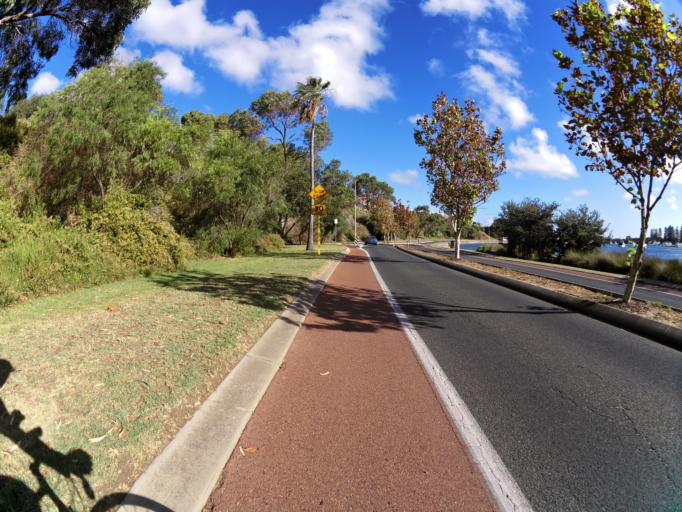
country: AU
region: Western Australia
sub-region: East Fremantle
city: East Fremantle
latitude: -32.0309
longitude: 115.7643
